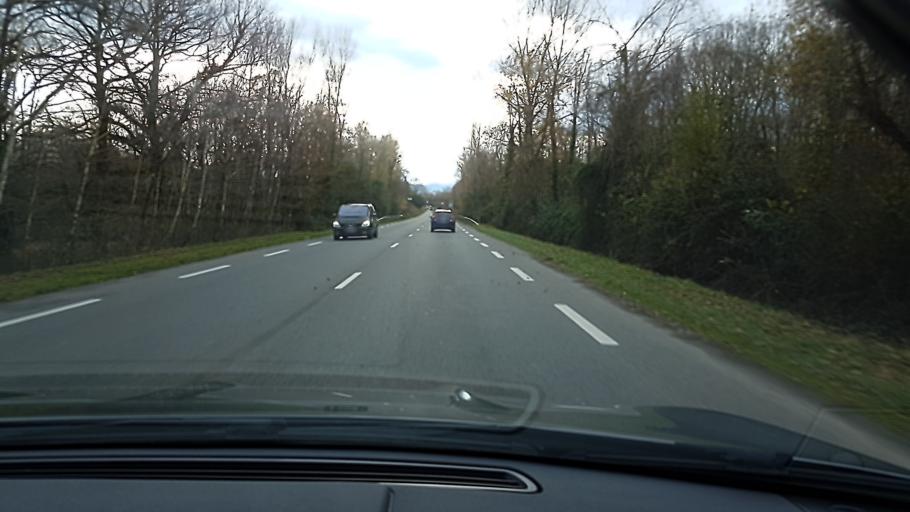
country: FR
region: Aquitaine
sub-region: Departement des Pyrenees-Atlantiques
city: Idron
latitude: 43.3112
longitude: -0.3048
